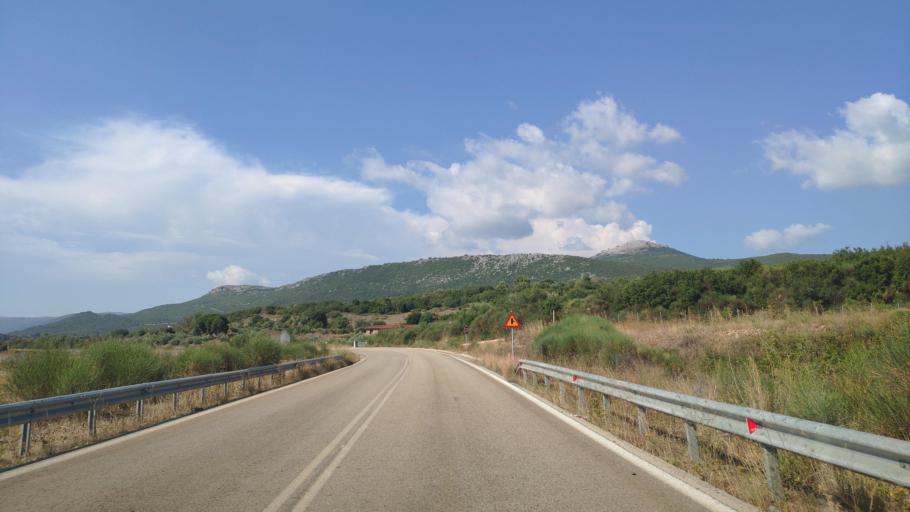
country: GR
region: West Greece
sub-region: Nomos Aitolias kai Akarnanias
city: Fitiai
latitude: 38.6757
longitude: 21.1557
